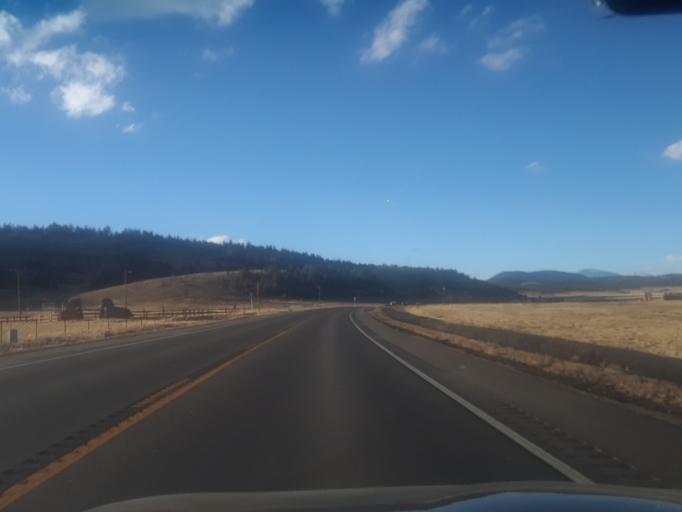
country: US
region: Colorado
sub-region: Park County
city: Fairplay
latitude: 39.0007
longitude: -105.9637
